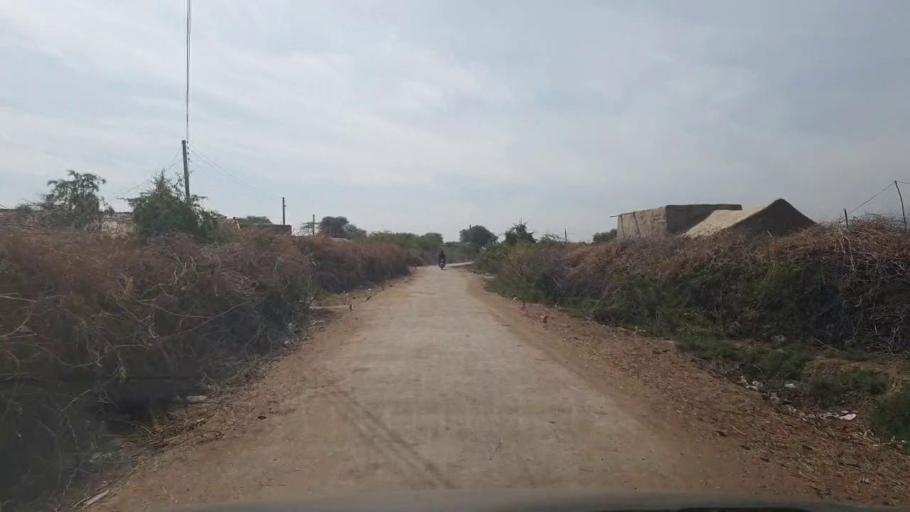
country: PK
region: Sindh
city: Kunri
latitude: 25.3230
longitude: 69.5924
